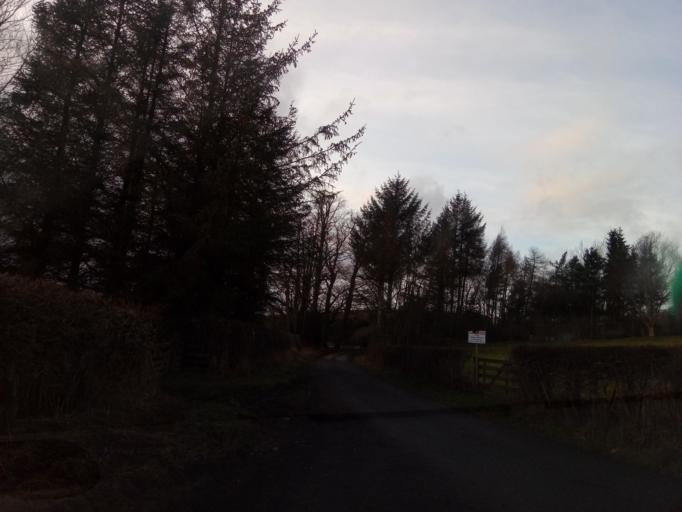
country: GB
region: Scotland
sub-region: The Scottish Borders
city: Newtown St Boswells
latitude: 55.5300
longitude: -2.7028
